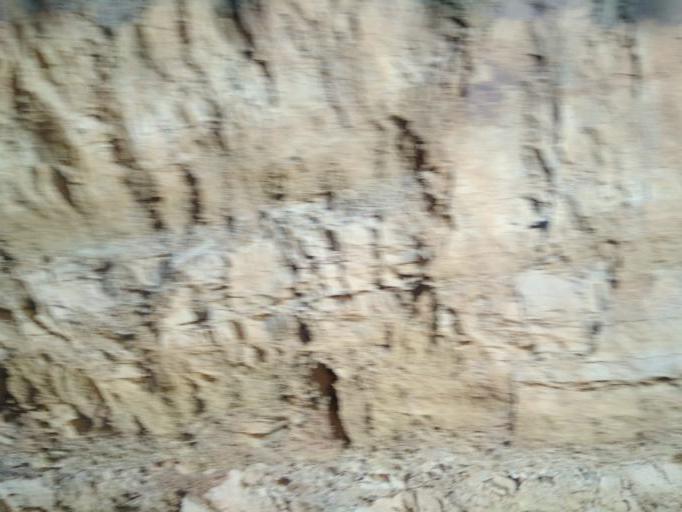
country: IL
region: Southern District
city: Eilat
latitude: 29.6105
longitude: 34.8764
